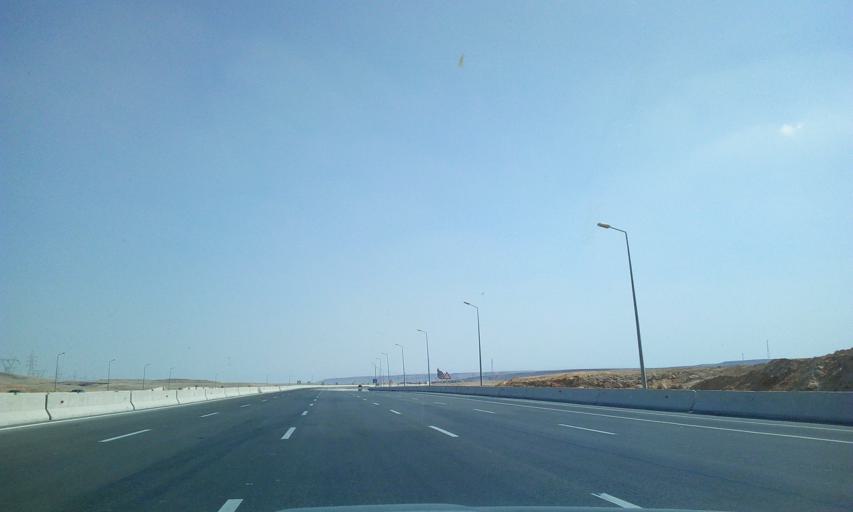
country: EG
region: As Suways
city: Ain Sukhna
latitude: 29.8146
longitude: 31.8948
